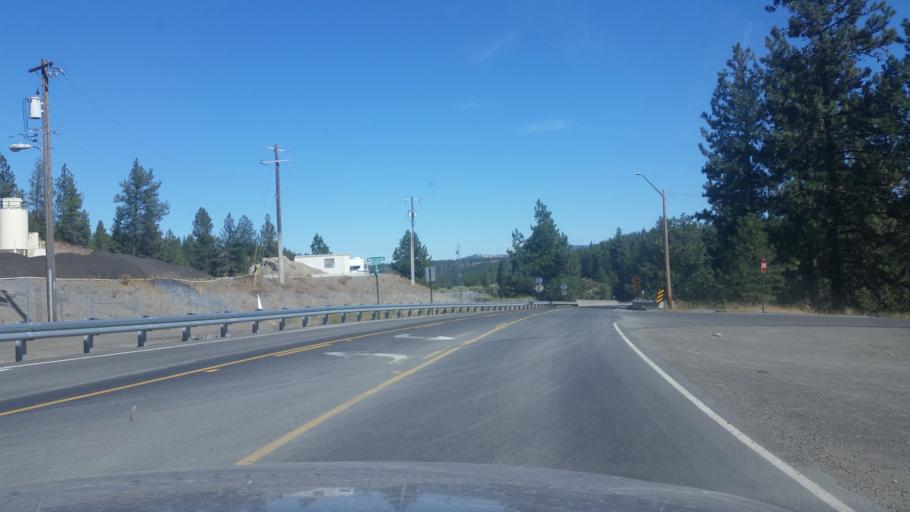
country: US
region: Washington
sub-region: Spokane County
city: Cheney
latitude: 47.5665
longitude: -117.4959
